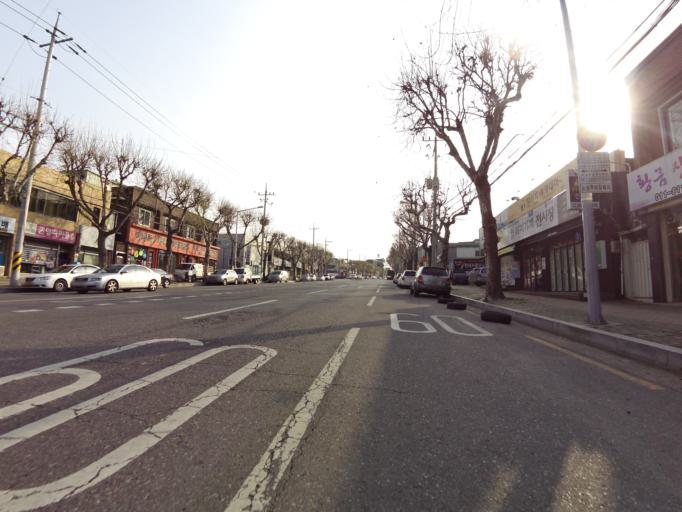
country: KR
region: Daegu
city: Daegu
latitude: 35.8678
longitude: 128.6456
